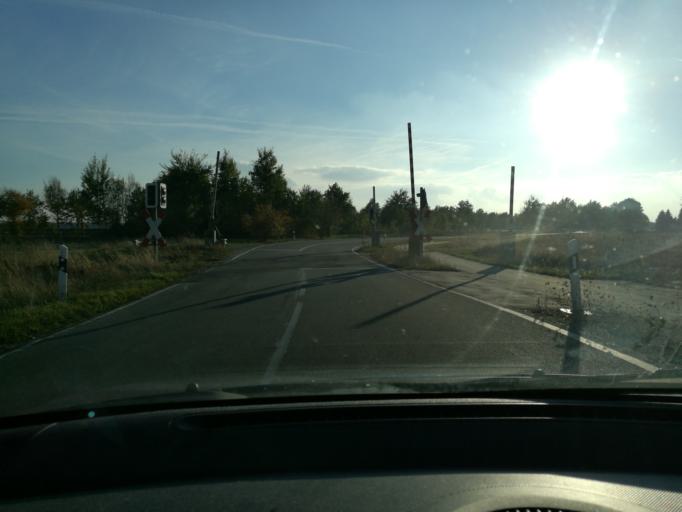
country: DE
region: Saxony-Anhalt
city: Luftkurort Arendsee
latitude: 52.8738
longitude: 11.4613
